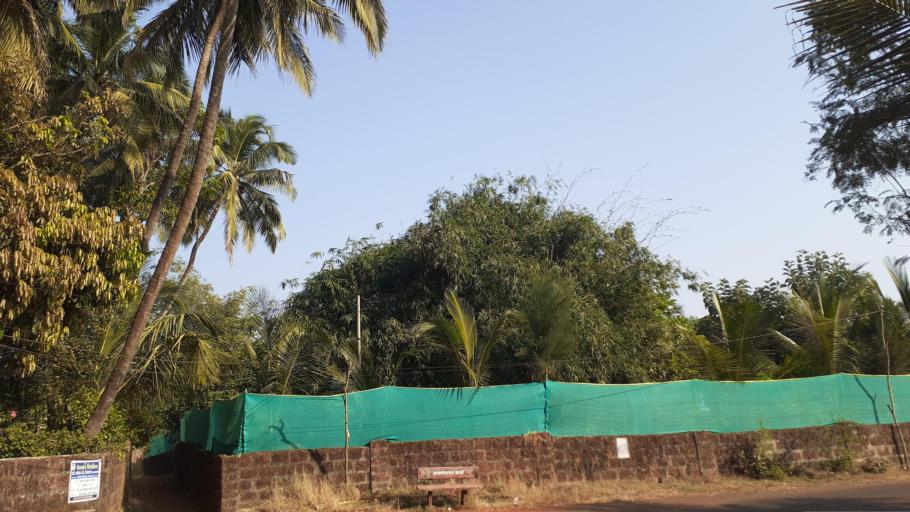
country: IN
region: Maharashtra
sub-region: Ratnagiri
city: Ratnagiri
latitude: 17.2123
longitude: 73.2489
